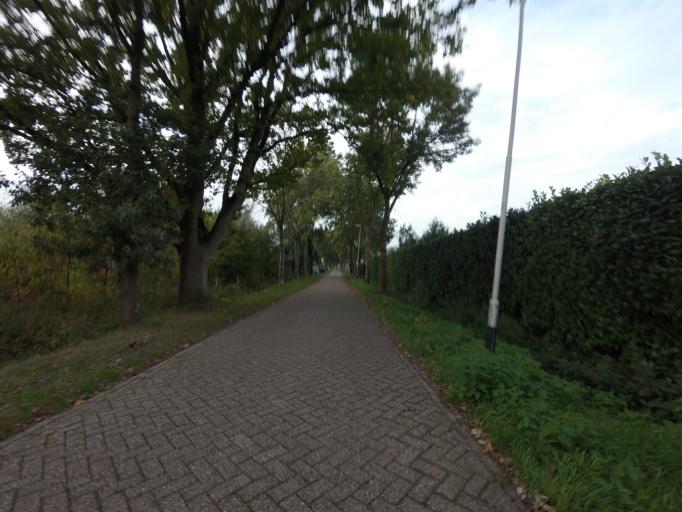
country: NL
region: North Brabant
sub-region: Gemeente Breda
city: Hoge Vucht
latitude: 51.6216
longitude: 4.7523
